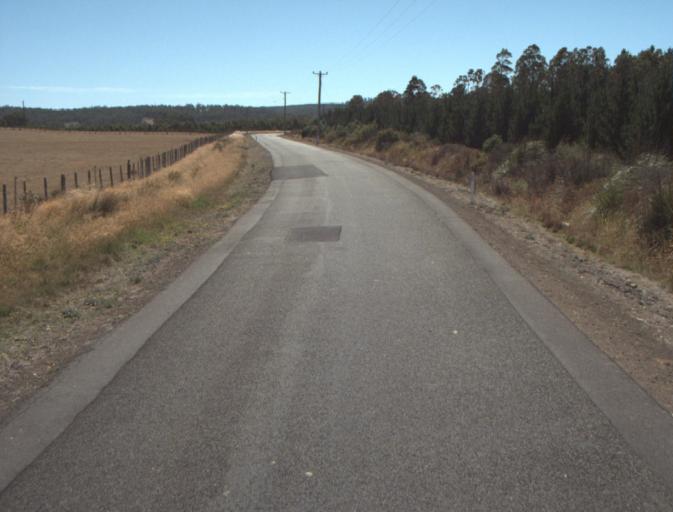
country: AU
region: Tasmania
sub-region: Launceston
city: Newstead
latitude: -41.3314
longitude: 147.3083
